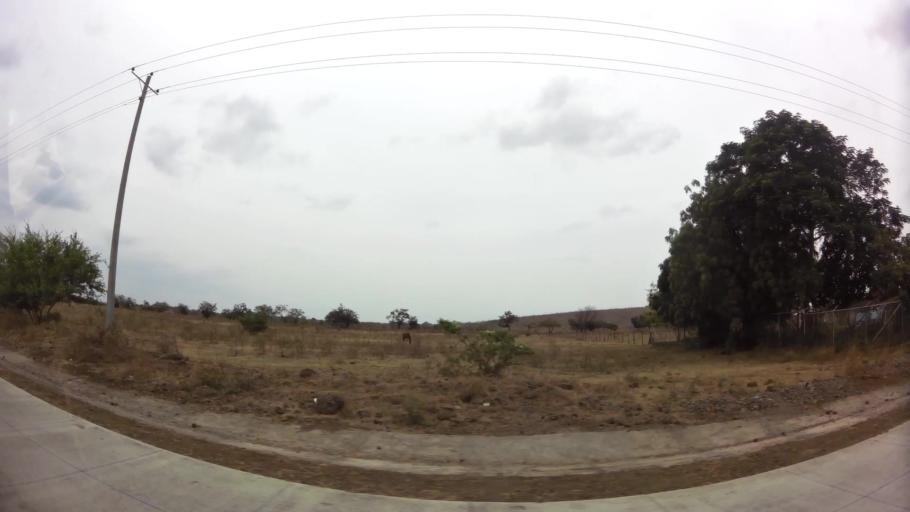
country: NI
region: Managua
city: Managua
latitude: 12.1049
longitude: -86.1750
